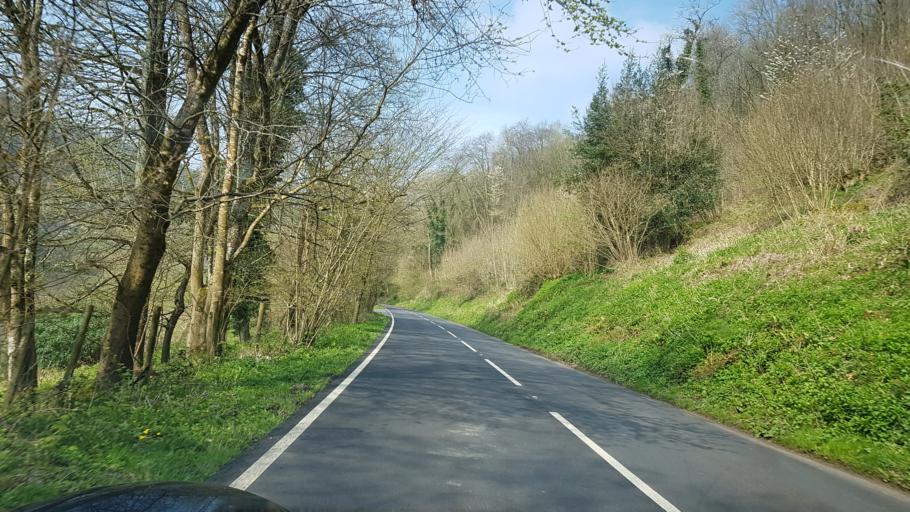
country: GB
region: Wales
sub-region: Monmouthshire
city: Monmouth
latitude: 51.7773
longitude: -2.6743
